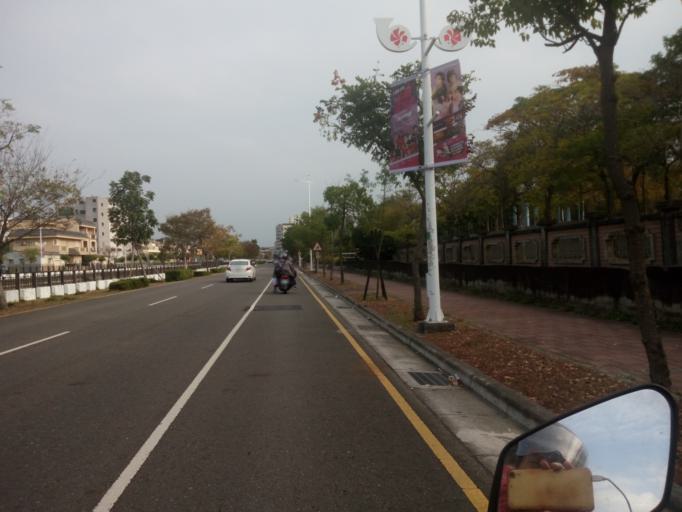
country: TW
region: Taiwan
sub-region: Chiayi
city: Jiayi Shi
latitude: 23.4807
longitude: 120.4229
